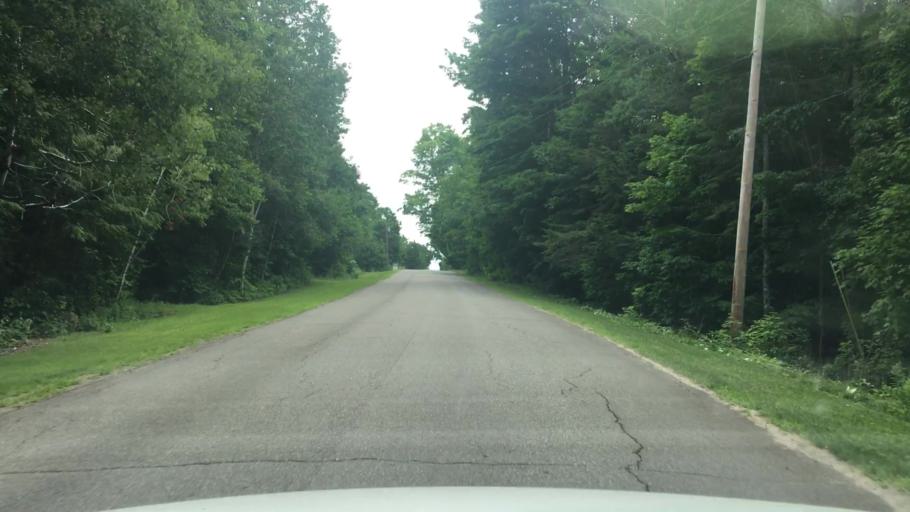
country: US
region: Maine
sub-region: Kennebec County
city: Albion
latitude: 44.4799
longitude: -69.3716
